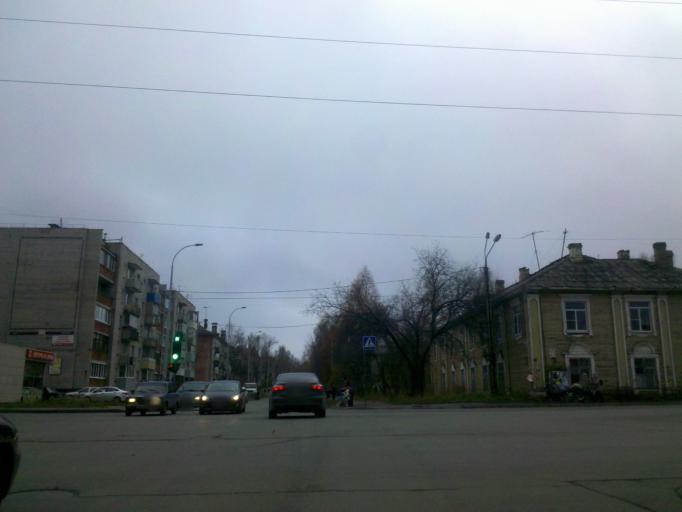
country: RU
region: Republic of Karelia
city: Petrozavodsk
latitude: 61.8032
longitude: 34.3352
